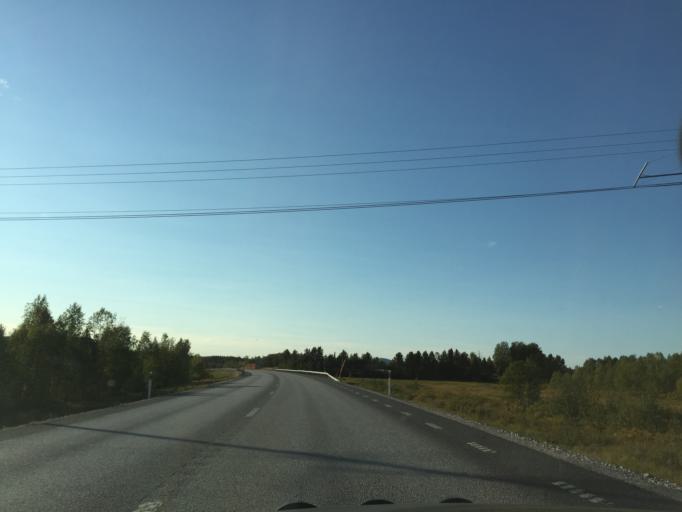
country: SE
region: Norrbotten
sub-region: Gallivare Kommun
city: Malmberget
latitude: 67.6437
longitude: 21.0508
